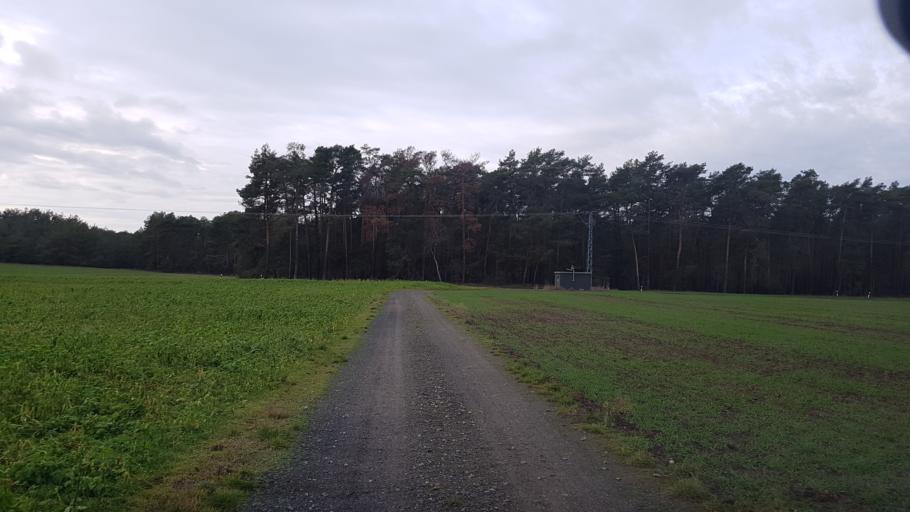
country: DE
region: Brandenburg
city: Hohenbucko
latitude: 51.7277
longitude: 13.4938
